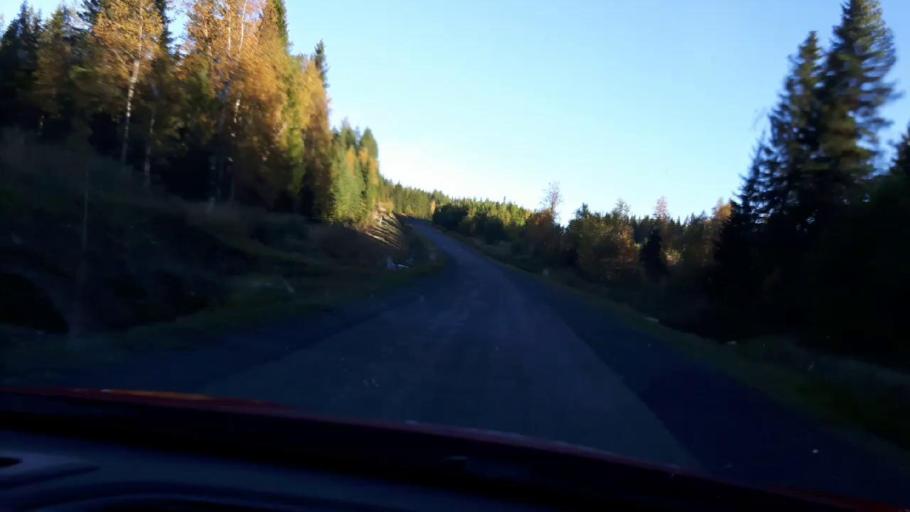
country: SE
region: Jaemtland
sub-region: OEstersunds Kommun
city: Lit
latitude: 63.5861
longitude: 14.8491
